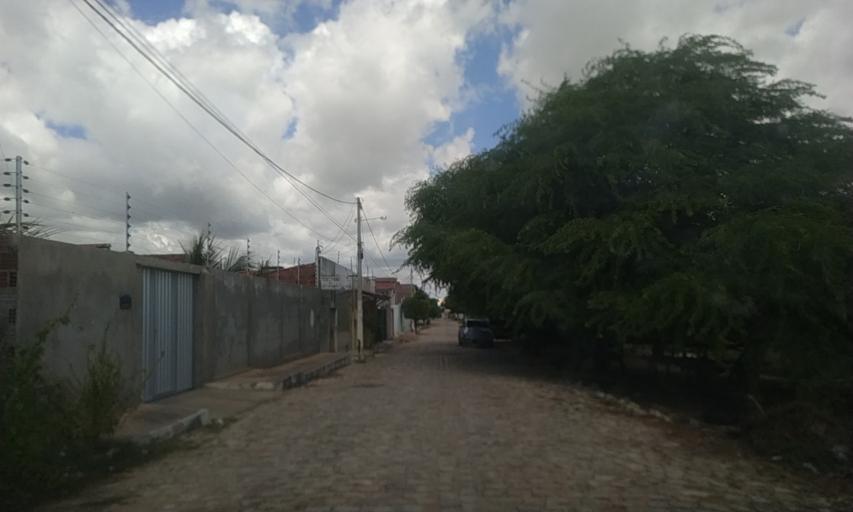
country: BR
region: Rio Grande do Norte
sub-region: Areia Branca
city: Areia Branca
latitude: -4.9269
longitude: -37.1106
